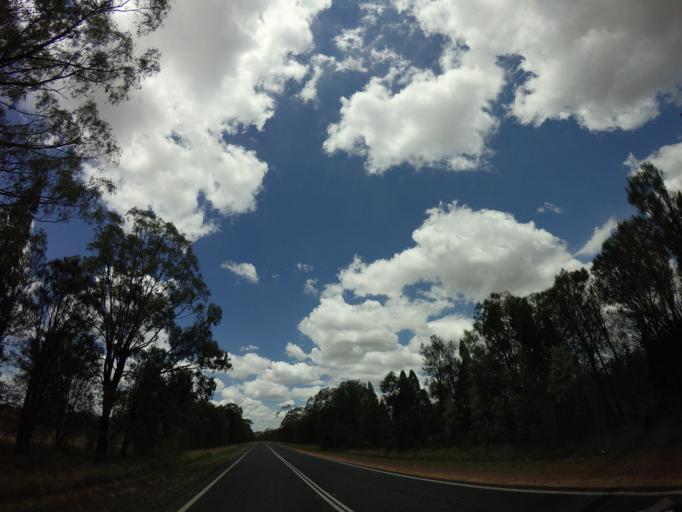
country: AU
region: Queensland
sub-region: Western Downs
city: Dalby
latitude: -27.9635
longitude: 151.1186
